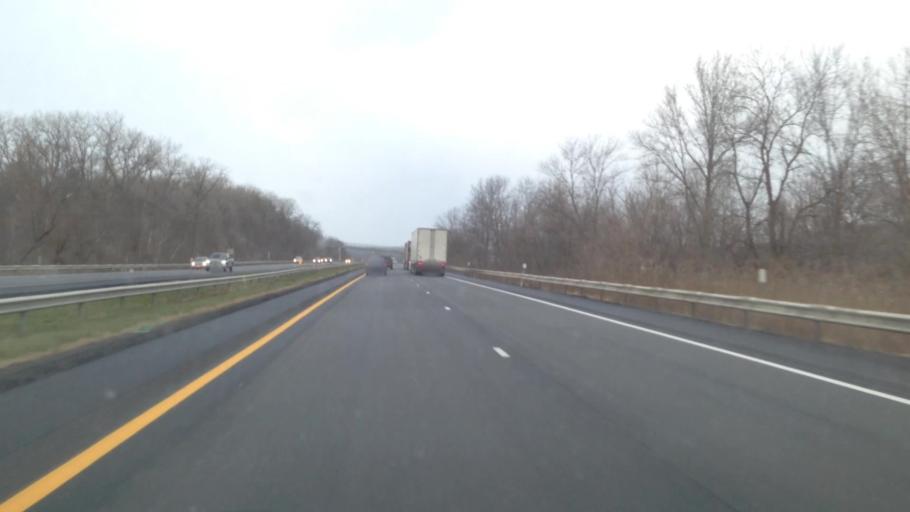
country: US
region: New York
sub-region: Montgomery County
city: Fonda
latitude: 42.9387
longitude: -74.3358
